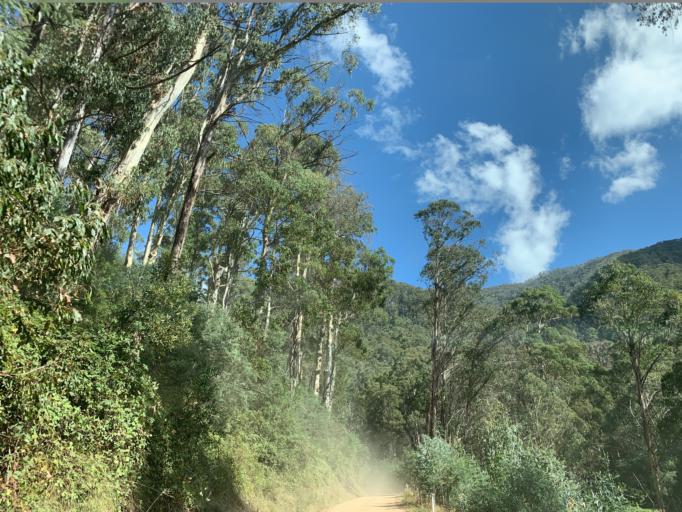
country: AU
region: Victoria
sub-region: Mansfield
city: Mansfield
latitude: -37.1037
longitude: 146.5019
